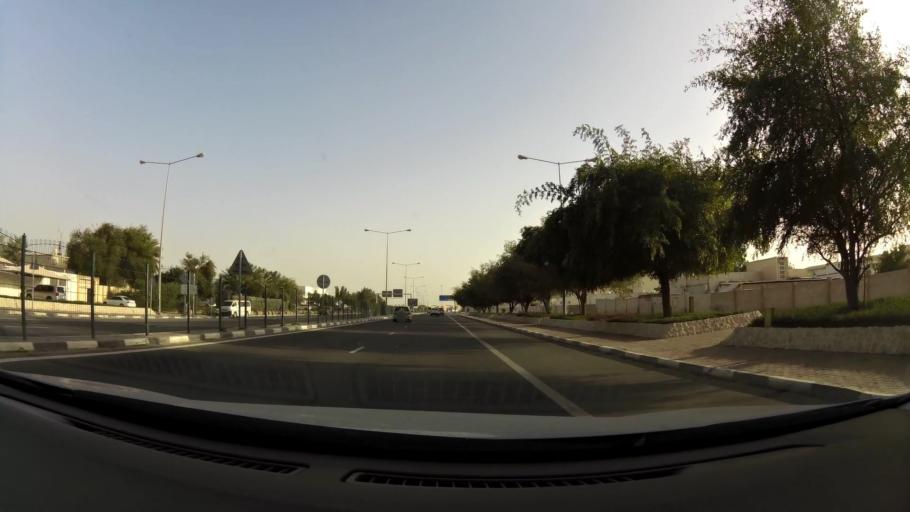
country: QA
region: Baladiyat ar Rayyan
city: Ar Rayyan
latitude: 25.3166
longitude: 51.4602
